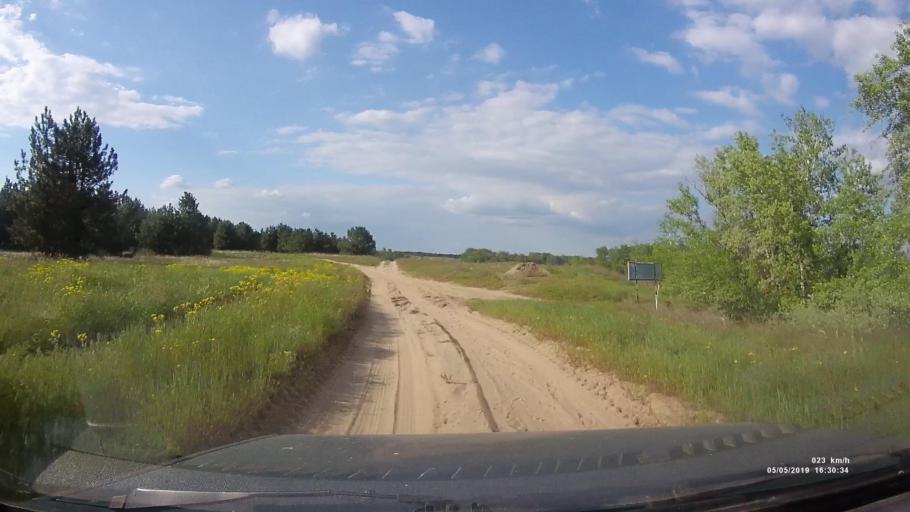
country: RU
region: Rostov
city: Ust'-Donetskiy
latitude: 47.7739
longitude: 41.0159
